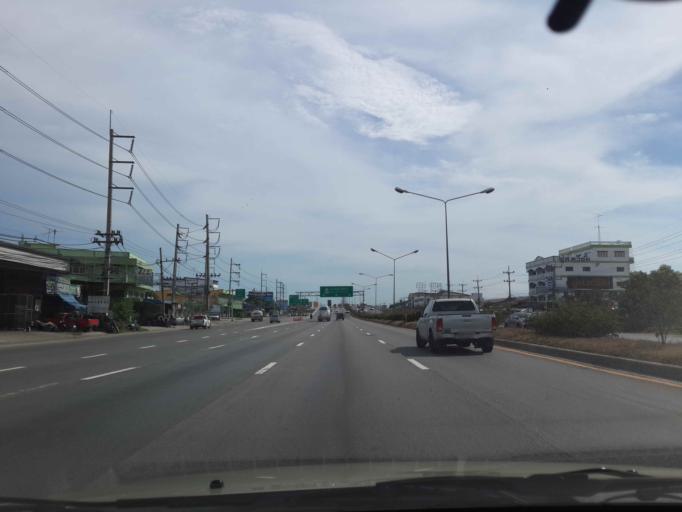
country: TH
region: Chon Buri
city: Chon Buri
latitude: 13.3559
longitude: 101.0085
